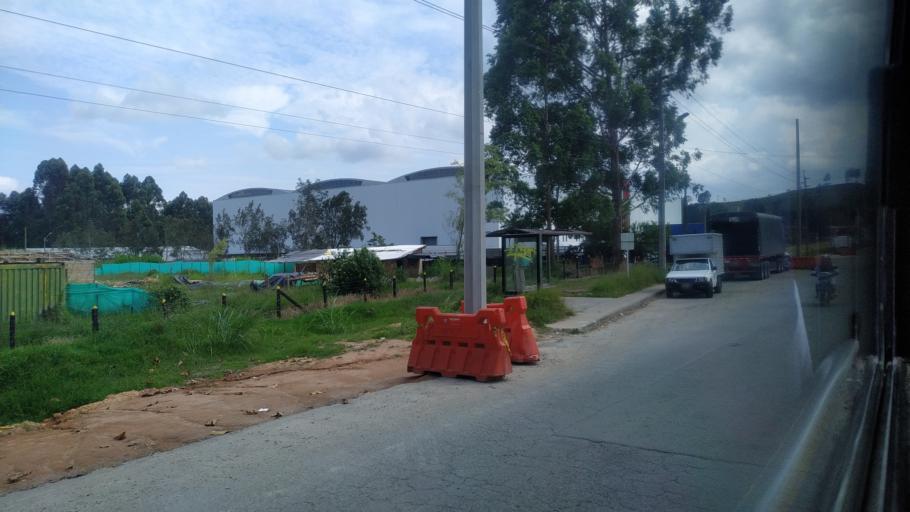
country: CO
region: Antioquia
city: Rionegro
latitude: 6.1766
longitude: -75.3686
